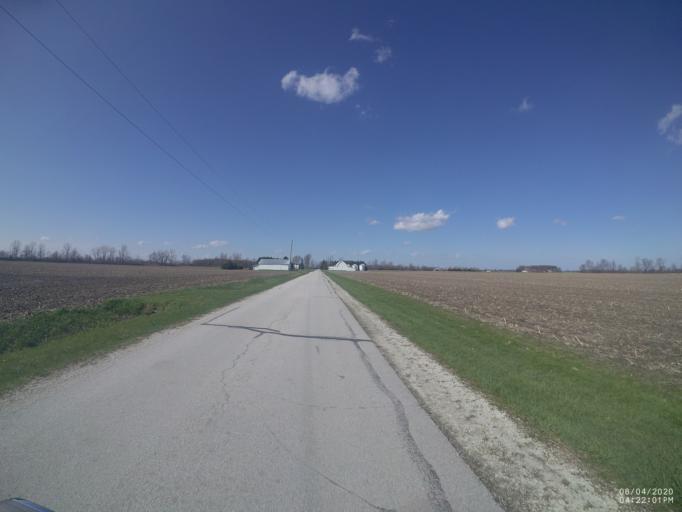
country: US
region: Ohio
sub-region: Sandusky County
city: Stony Prairie
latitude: 41.2836
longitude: -83.2165
